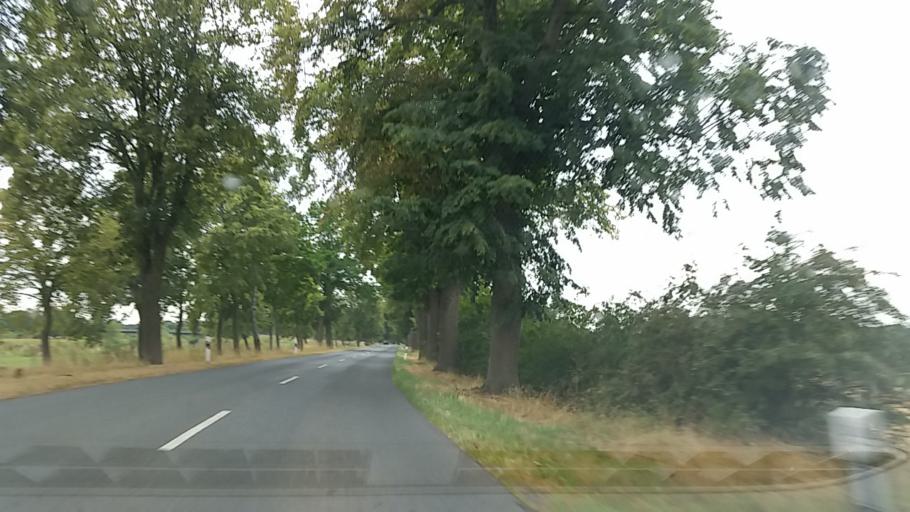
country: DE
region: Lower Saxony
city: Gilten
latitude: 52.6996
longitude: 9.5977
